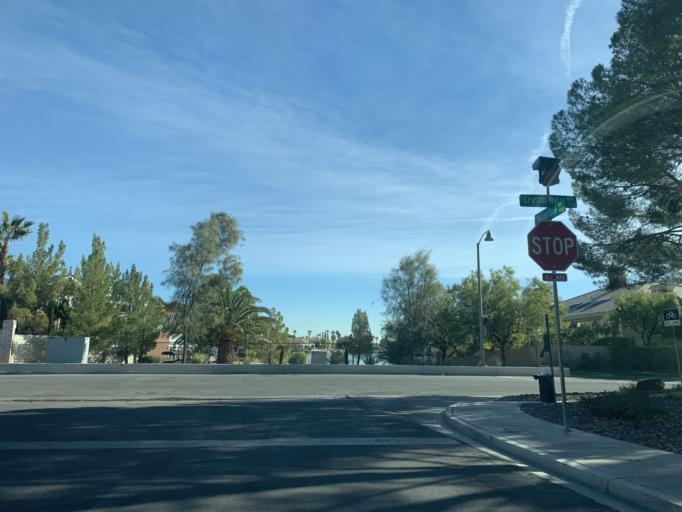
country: US
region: Nevada
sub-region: Clark County
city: Summerlin South
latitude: 36.1371
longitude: -115.2893
